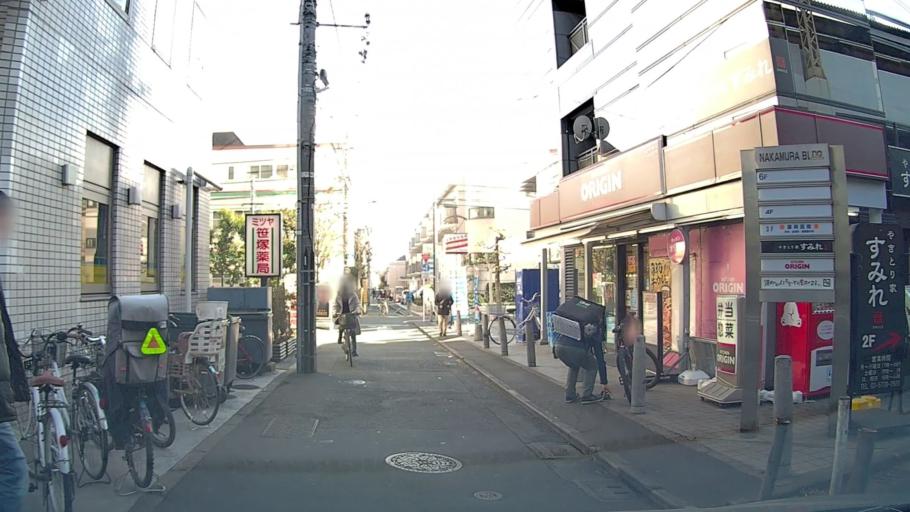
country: JP
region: Tokyo
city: Tokyo
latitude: 35.6735
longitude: 139.6667
